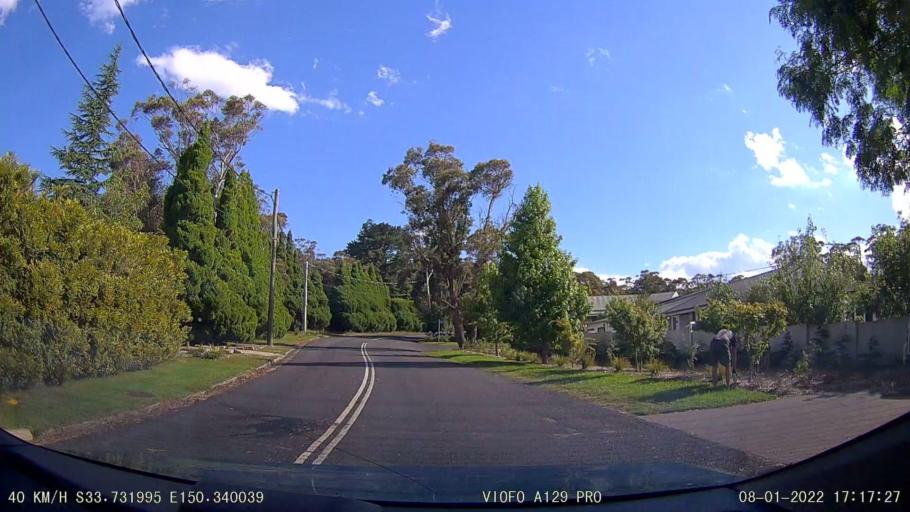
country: AU
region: New South Wales
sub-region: Blue Mountains Municipality
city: Leura
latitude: -33.7320
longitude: 150.3401
